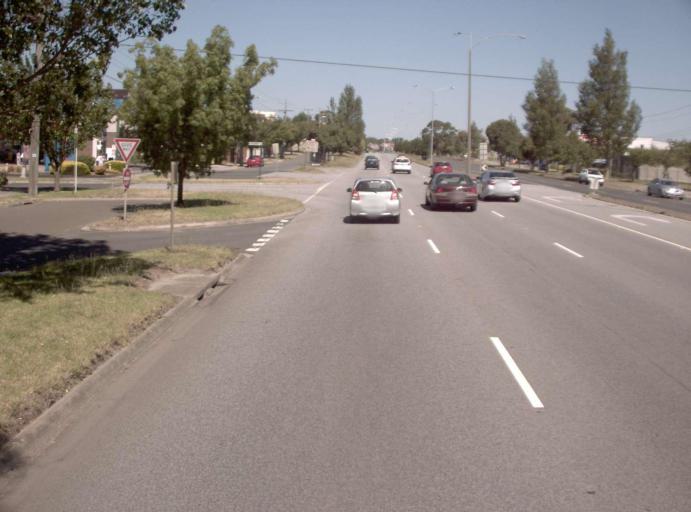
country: AU
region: Victoria
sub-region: Monash
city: Clayton
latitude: -37.9276
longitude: 145.1484
